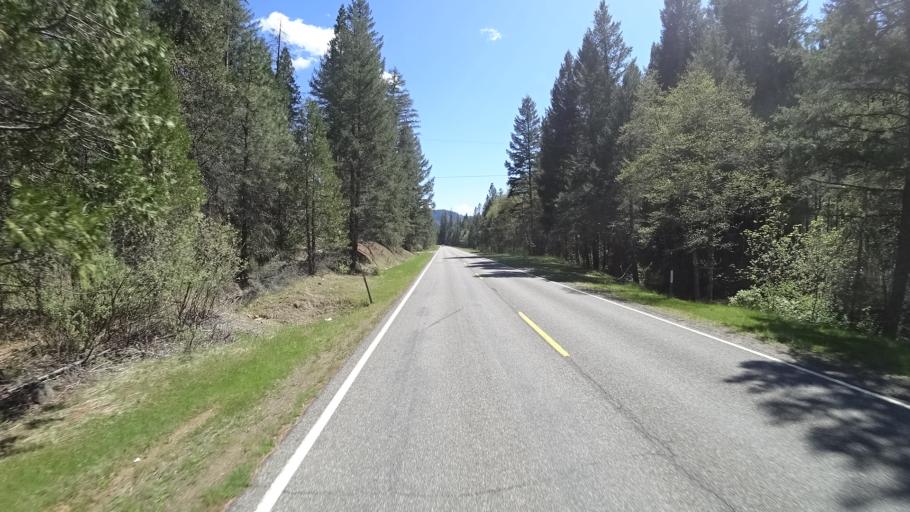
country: US
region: California
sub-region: Trinity County
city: Weaverville
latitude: 40.7744
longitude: -122.8922
